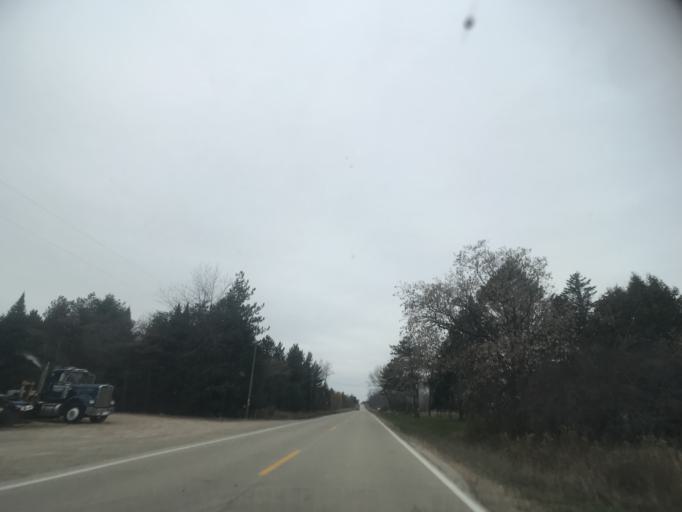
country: US
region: Wisconsin
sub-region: Oconto County
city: Gillett
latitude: 44.9833
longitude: -88.3008
